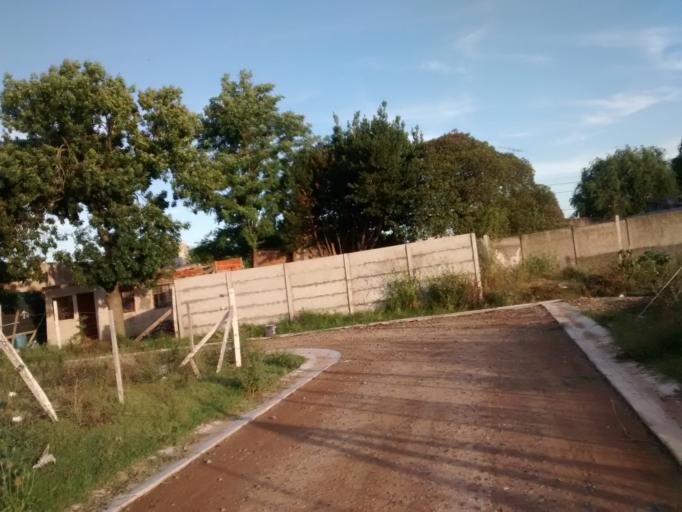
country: AR
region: Buenos Aires
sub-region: Partido de La Plata
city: La Plata
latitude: -34.9540
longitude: -57.9370
